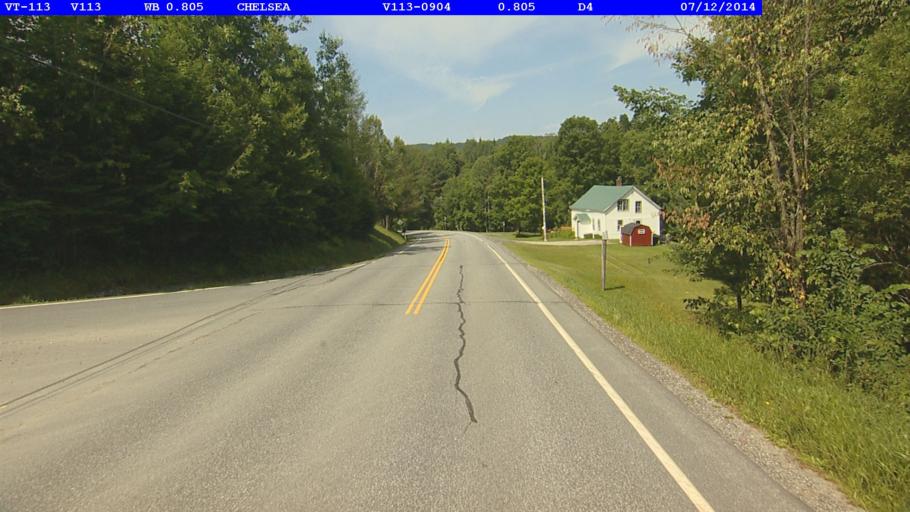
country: US
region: Vermont
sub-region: Orange County
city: Chelsea
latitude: 43.9927
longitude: -72.4345
